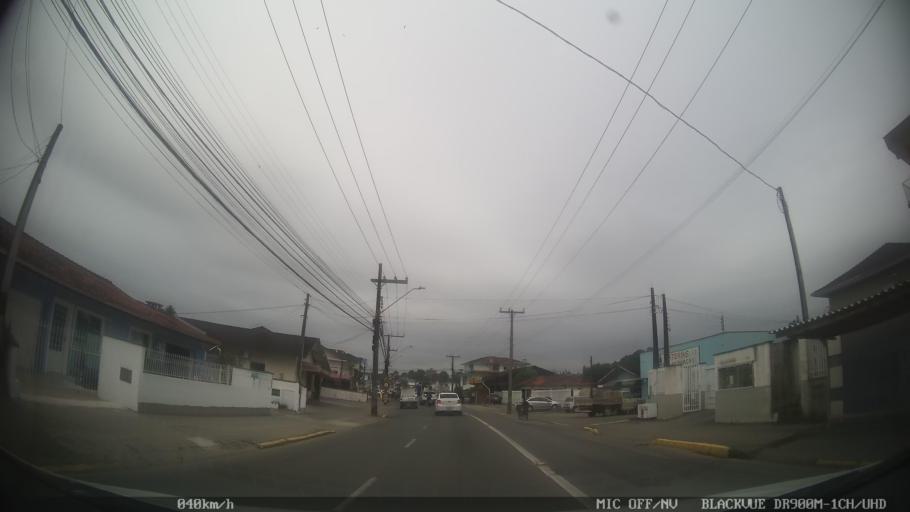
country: BR
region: Santa Catarina
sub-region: Joinville
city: Joinville
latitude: -26.2745
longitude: -48.8327
